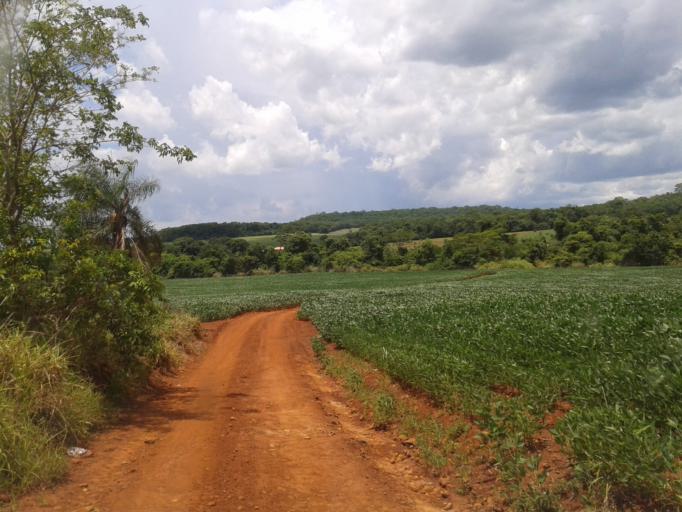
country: BR
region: Minas Gerais
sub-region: Centralina
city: Centralina
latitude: -18.6812
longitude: -49.2180
